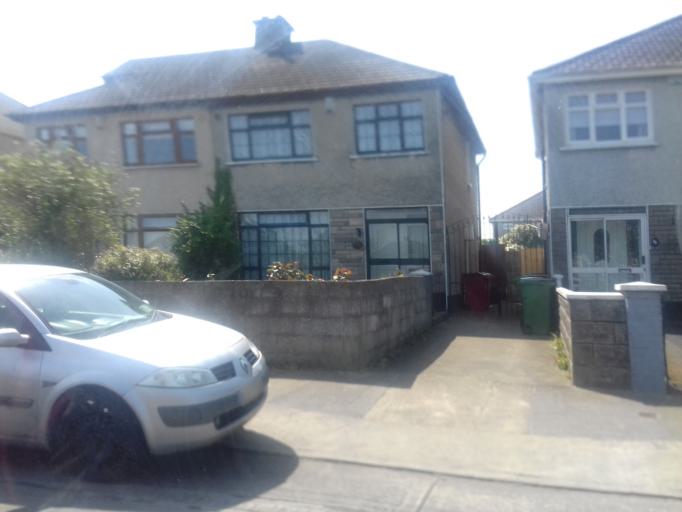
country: IE
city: Bonnybrook
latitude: 53.4005
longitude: -6.2103
